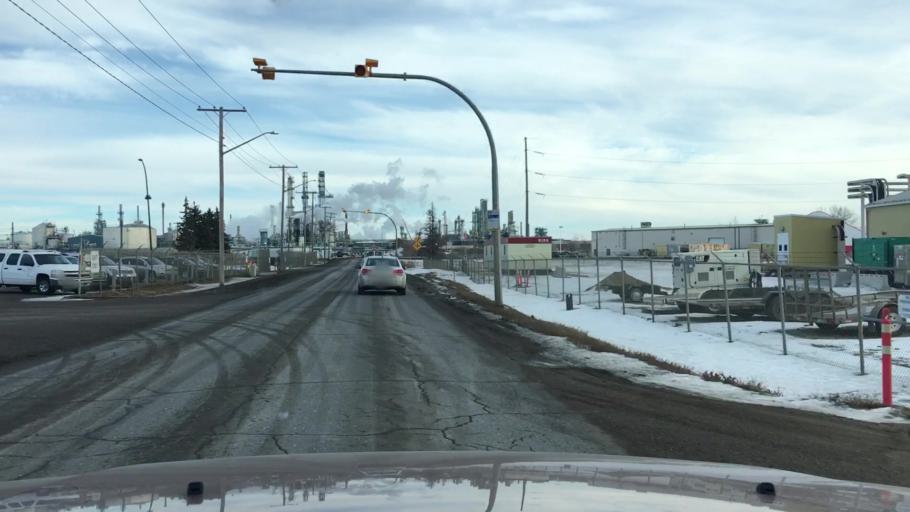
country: CA
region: Saskatchewan
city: Regina
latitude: 50.4843
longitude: -104.5855
